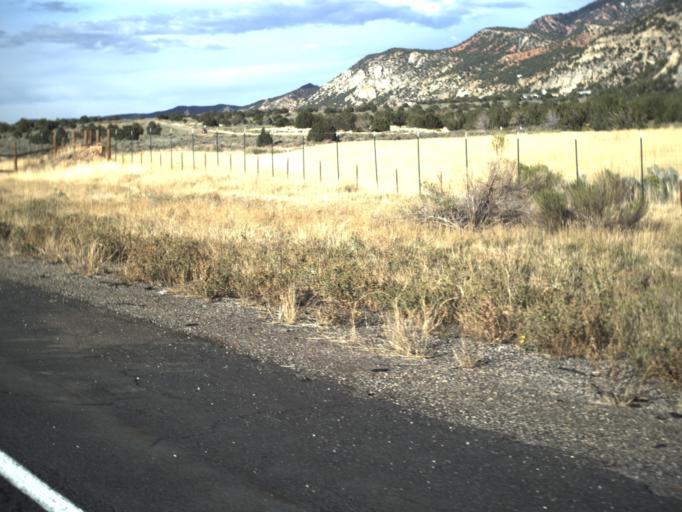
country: US
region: Utah
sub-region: Washington County
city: Toquerville
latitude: 37.4861
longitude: -113.2193
